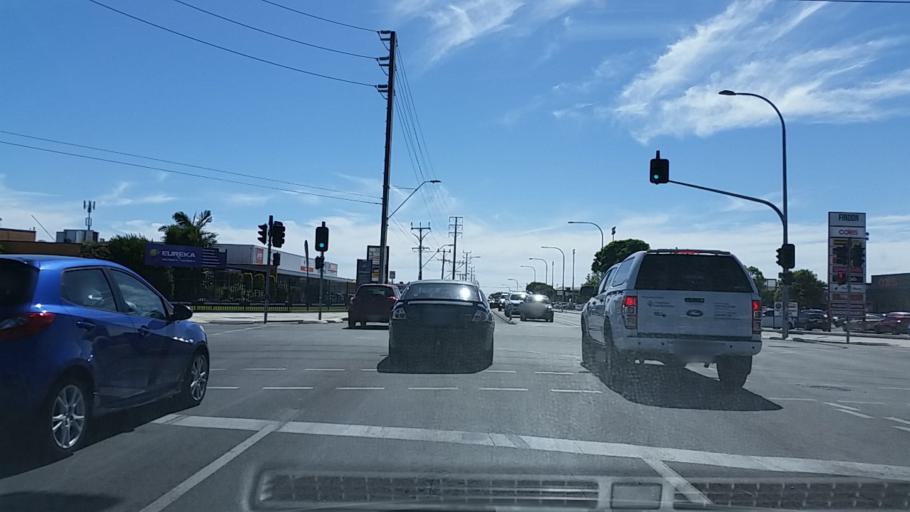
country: AU
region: South Australia
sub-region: Charles Sturt
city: Findon
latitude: -34.9055
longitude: 138.5328
